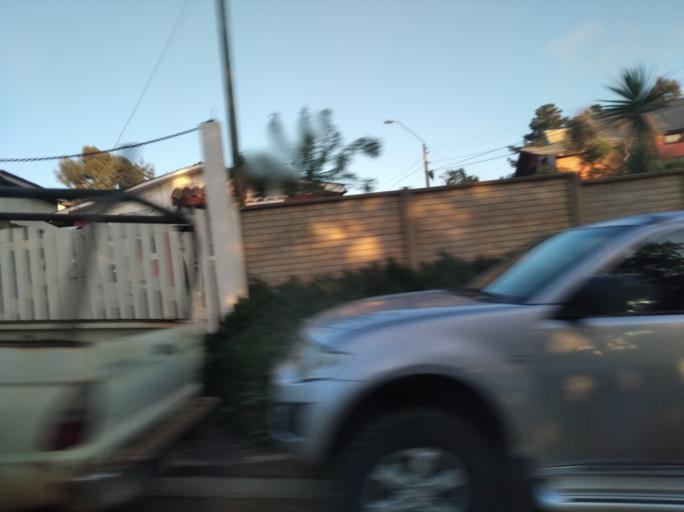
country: CL
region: Valparaiso
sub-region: San Antonio Province
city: El Tabo
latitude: -33.4549
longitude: -71.6595
